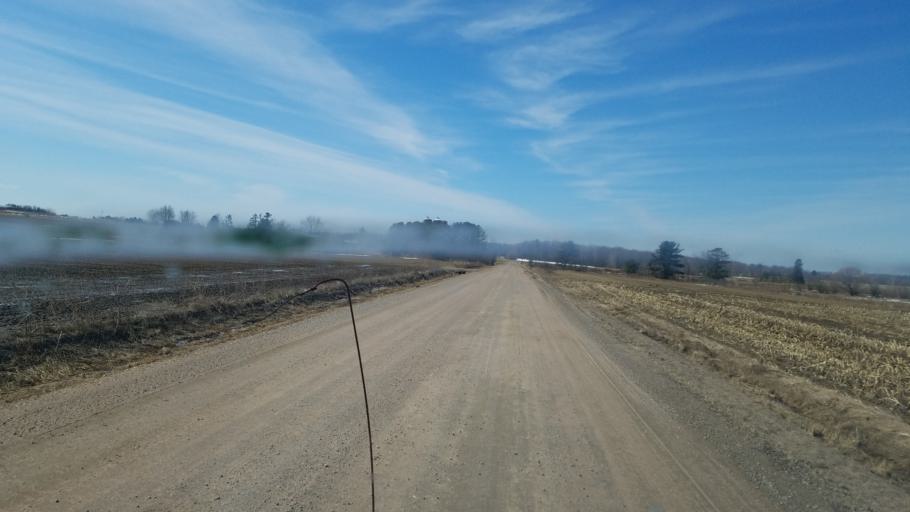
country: US
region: Wisconsin
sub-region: Clark County
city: Loyal
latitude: 44.6110
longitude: -90.4500
